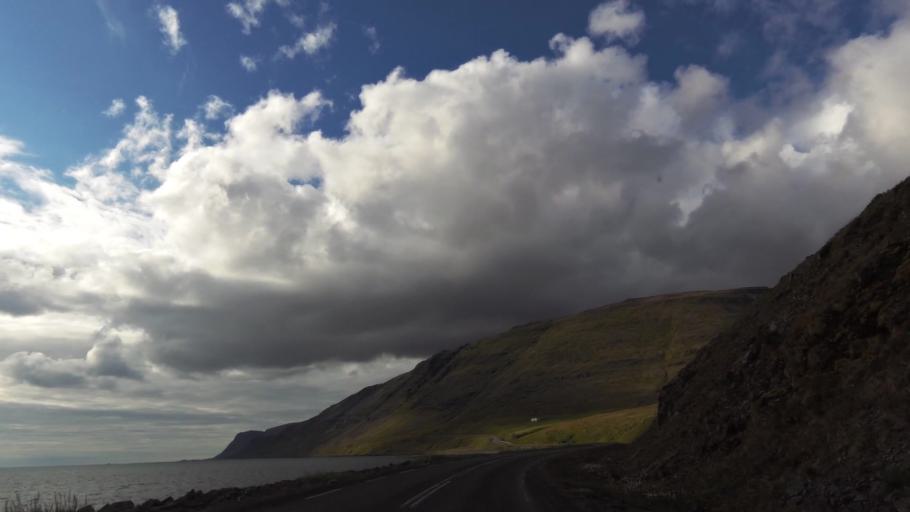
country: IS
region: West
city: Olafsvik
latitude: 65.5474
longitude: -23.8878
